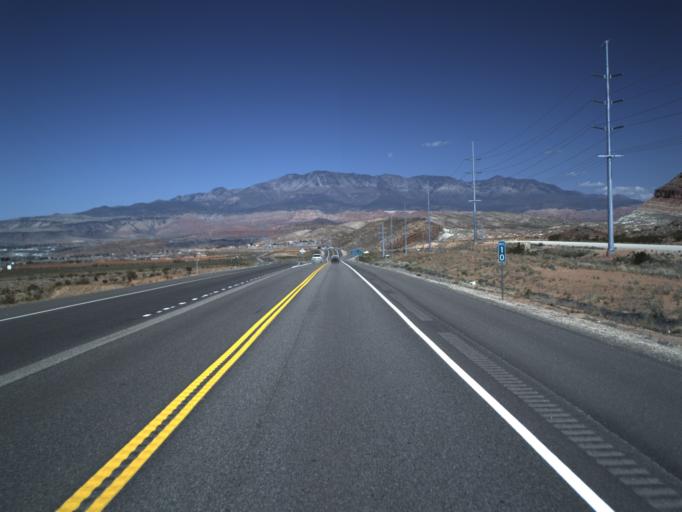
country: US
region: Utah
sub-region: Washington County
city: Washington
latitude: 37.0510
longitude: -113.4857
